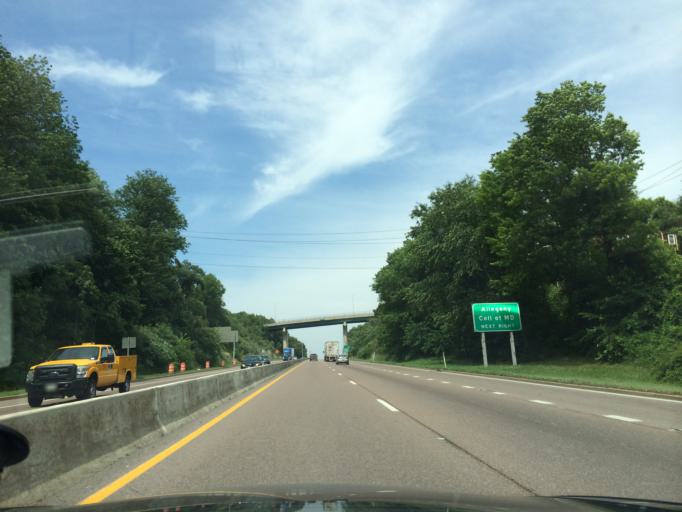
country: US
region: Maryland
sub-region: Allegany County
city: Cumberland
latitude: 39.6521
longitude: -78.7532
